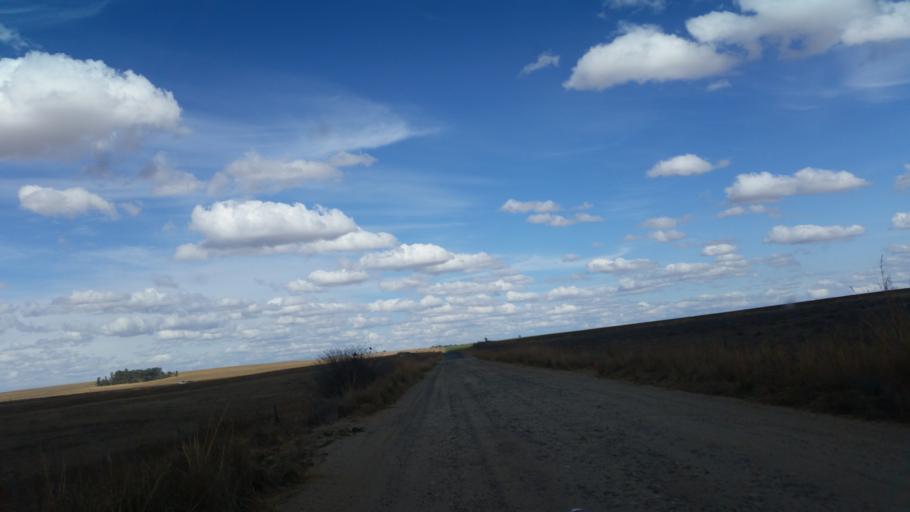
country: ZA
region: Orange Free State
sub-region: Thabo Mofutsanyana District Municipality
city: Bethlehem
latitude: -28.1598
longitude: 28.6767
